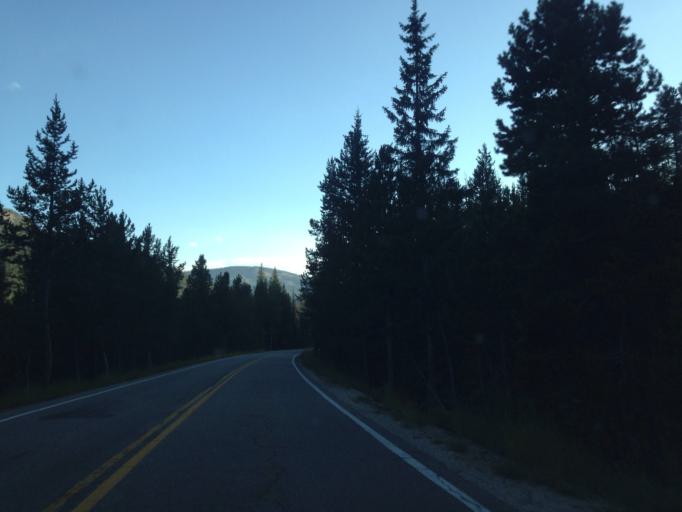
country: US
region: Utah
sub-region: Summit County
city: Kamas
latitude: 40.6366
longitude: -110.9519
